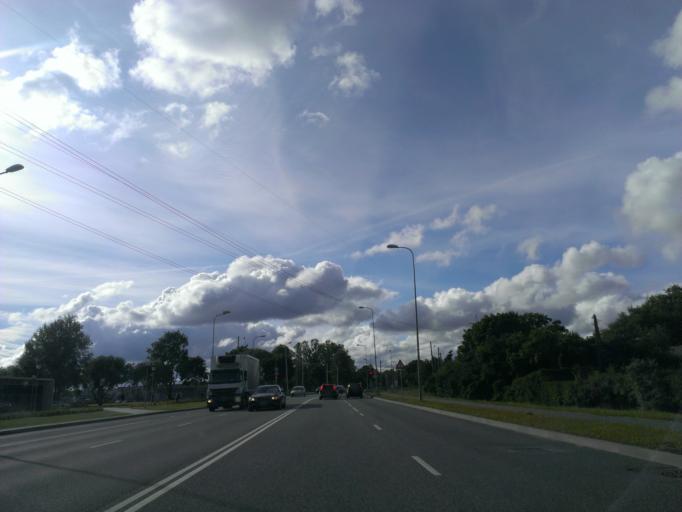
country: LV
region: Stopini
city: Ulbroka
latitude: 56.9575
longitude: 24.2401
